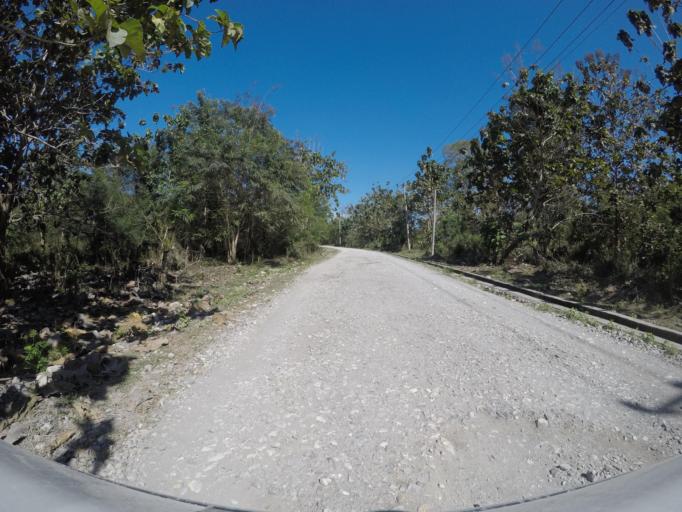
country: TL
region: Viqueque
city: Viqueque
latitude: -8.9719
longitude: 126.0583
